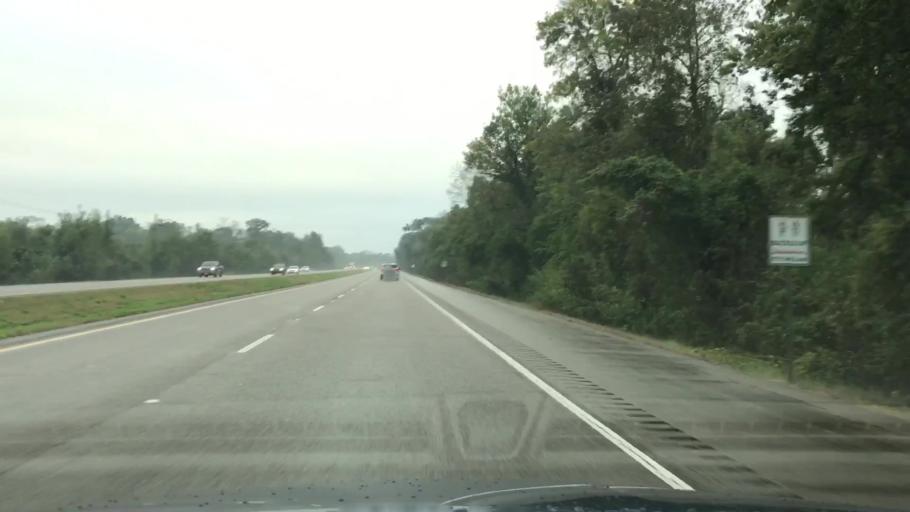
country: US
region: Louisiana
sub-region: Saint Charles Parish
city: Paradis
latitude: 29.8523
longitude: -90.4480
